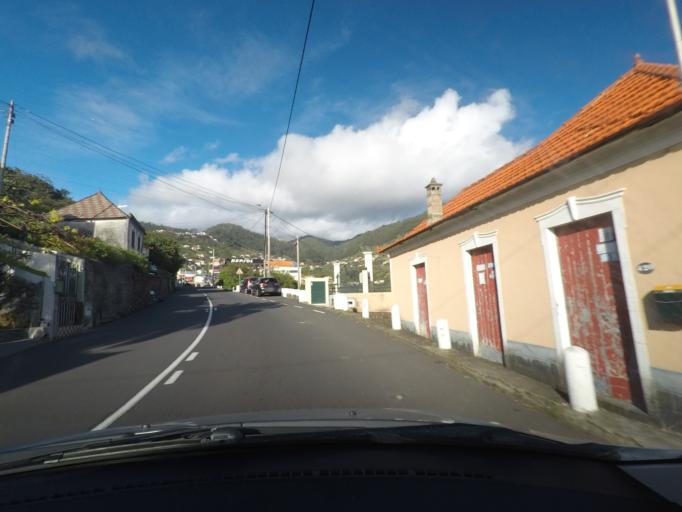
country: PT
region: Madeira
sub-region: Ribeira Brava
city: Campanario
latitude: 32.6697
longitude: -17.0306
